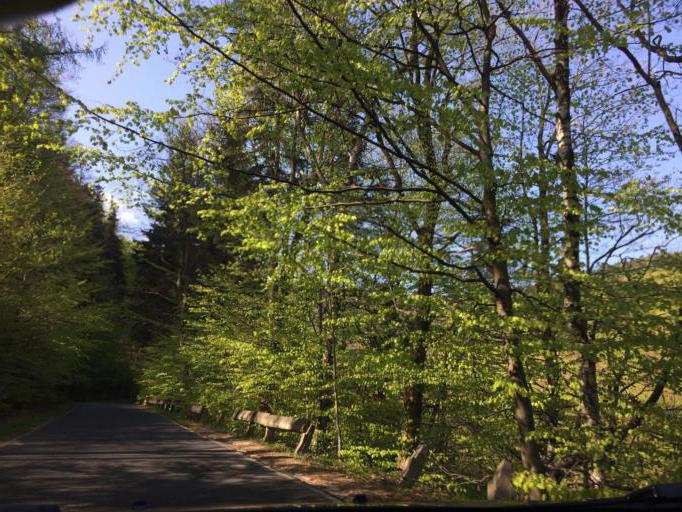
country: PL
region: Lower Silesian Voivodeship
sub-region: Powiat klodzki
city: Jugow
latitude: 50.6644
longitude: 16.5346
